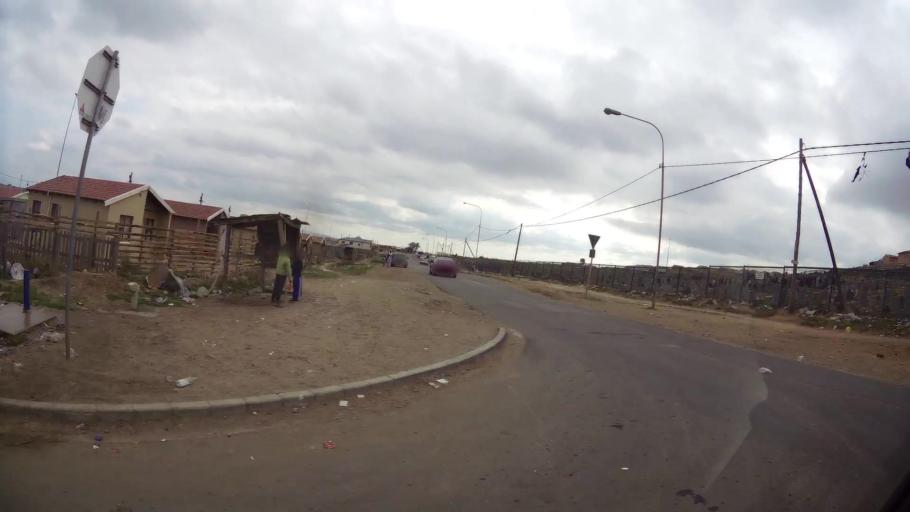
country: ZA
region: Eastern Cape
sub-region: Nelson Mandela Bay Metropolitan Municipality
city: Port Elizabeth
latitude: -33.8812
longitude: 25.5529
